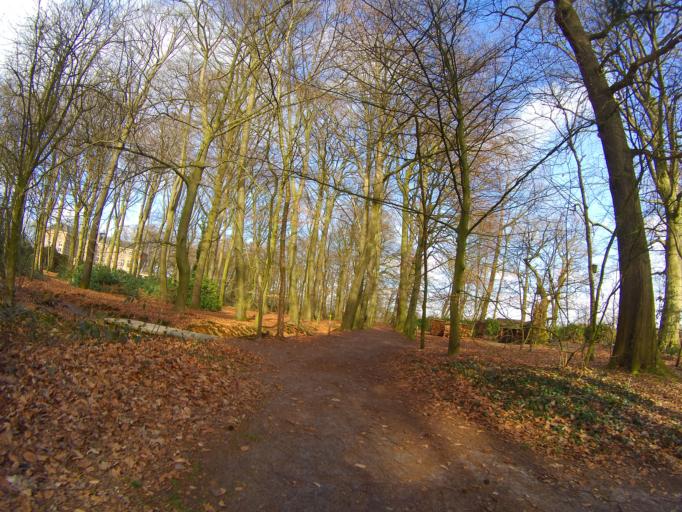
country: NL
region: Utrecht
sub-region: Gemeente Leusden
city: Leusden
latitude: 52.1515
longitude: 5.4511
